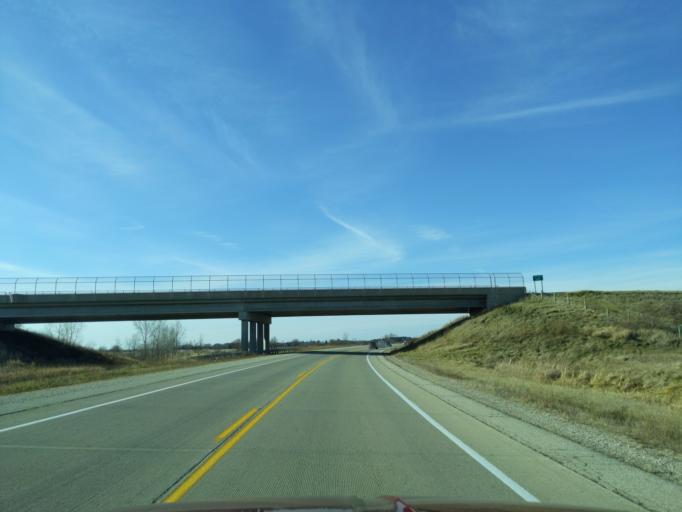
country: US
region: Wisconsin
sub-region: Walworth County
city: Whitewater
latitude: 42.8224
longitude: -88.7627
